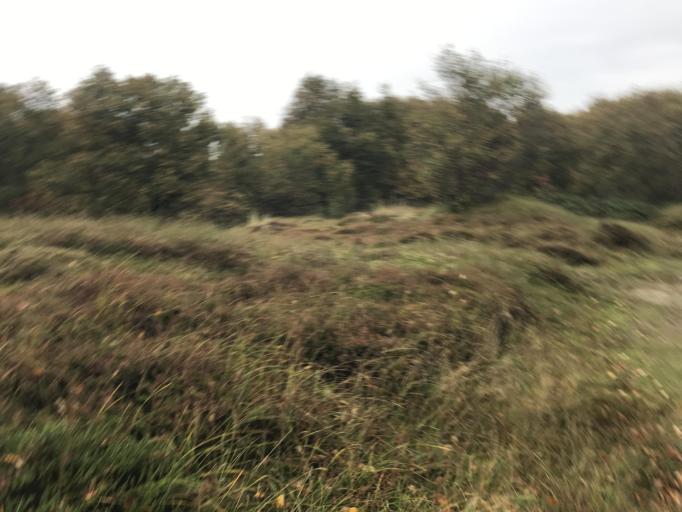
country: DE
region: Lower Saxony
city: Borkum
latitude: 53.5750
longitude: 6.6854
